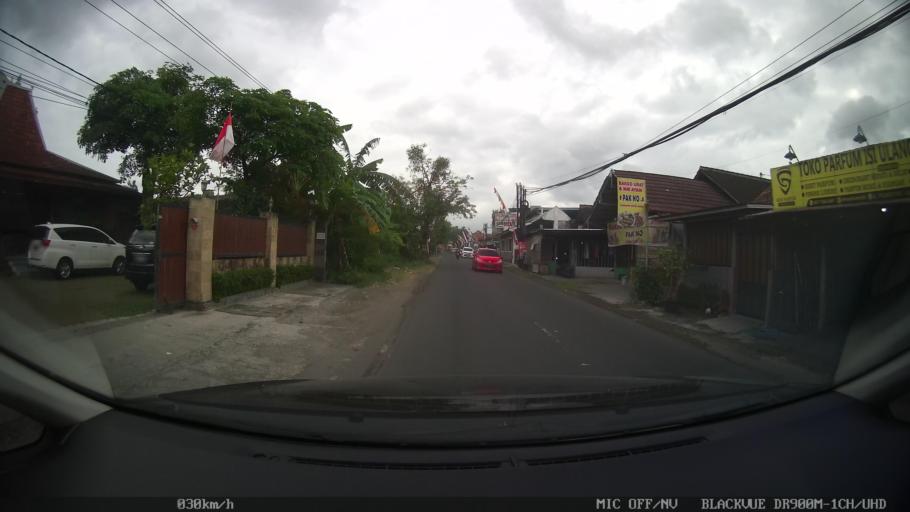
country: ID
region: Daerah Istimewa Yogyakarta
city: Sewon
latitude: -7.8327
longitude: 110.4125
